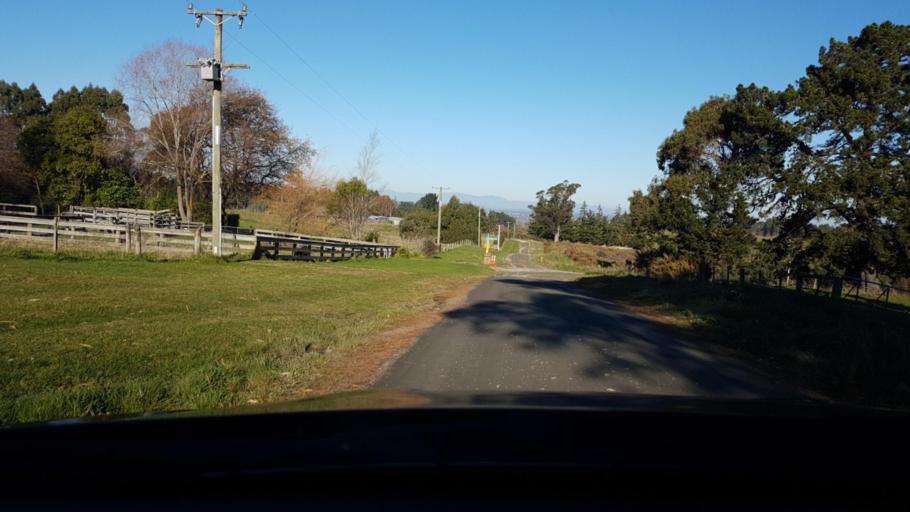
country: NZ
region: Canterbury
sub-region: Waimakariri District
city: Woodend
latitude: -43.2469
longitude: 172.5755
